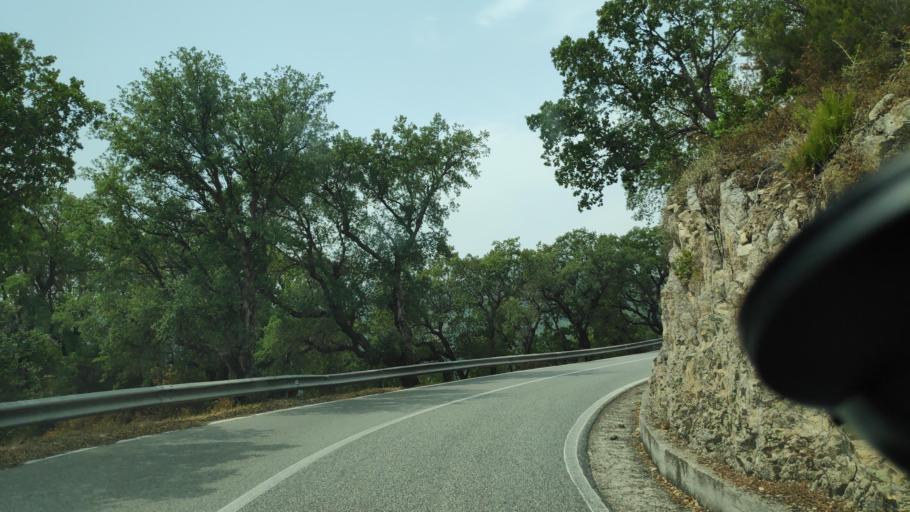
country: IT
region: Calabria
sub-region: Provincia di Catanzaro
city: San Sostene
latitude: 38.6368
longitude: 16.5094
